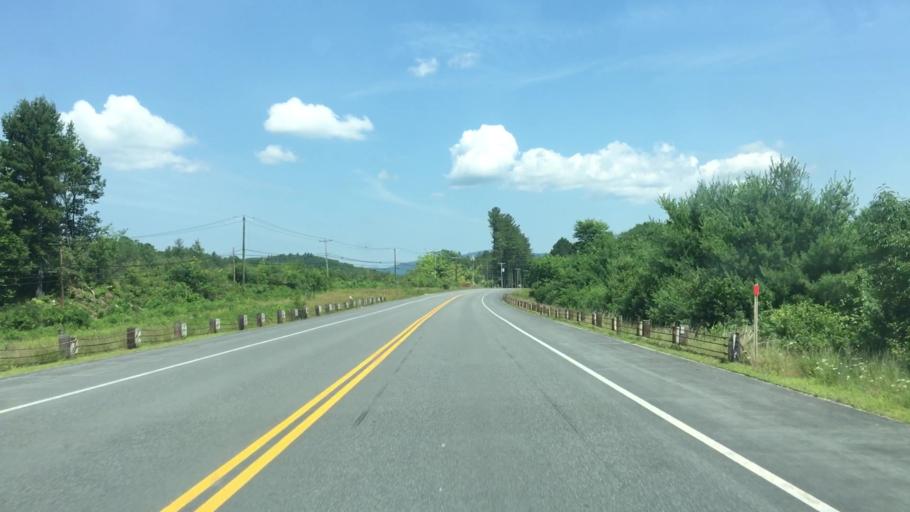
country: US
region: New Hampshire
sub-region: Sullivan County
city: Newport
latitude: 43.3827
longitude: -72.1813
